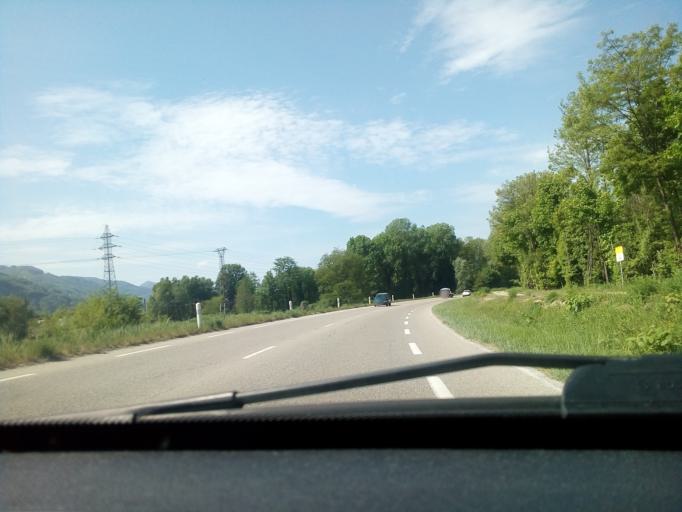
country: FR
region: Rhone-Alpes
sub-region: Departement de l'Isere
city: Froges
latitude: 45.2676
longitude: 5.9104
